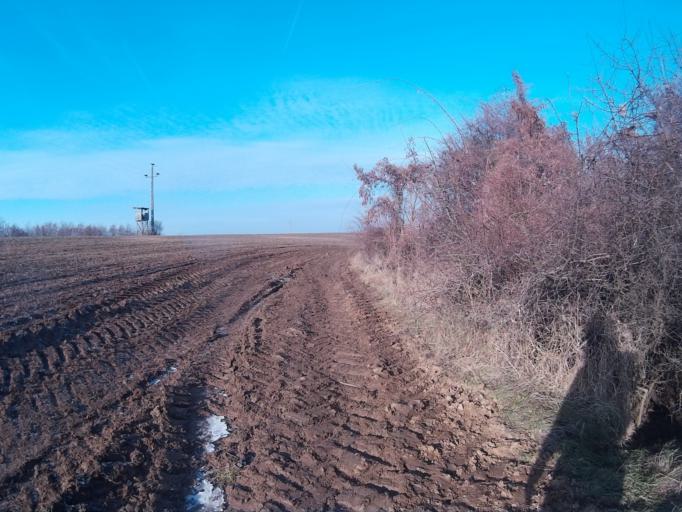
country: HU
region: Nograd
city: Bercel
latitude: 47.9367
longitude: 19.4279
